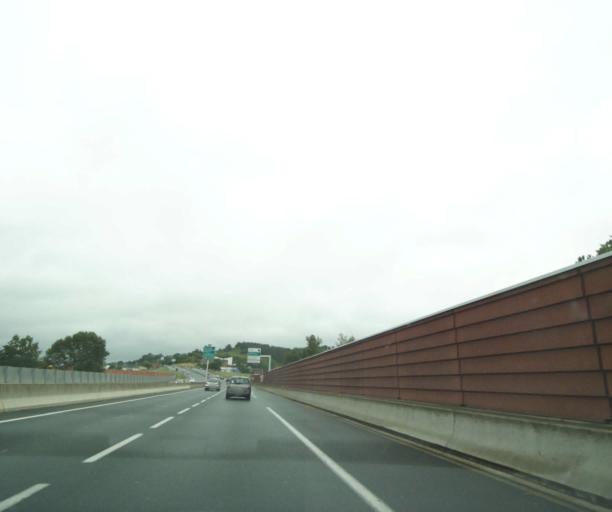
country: FR
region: Midi-Pyrenees
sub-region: Departement du Tarn
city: Le Sequestre
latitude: 43.9110
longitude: 2.1361
